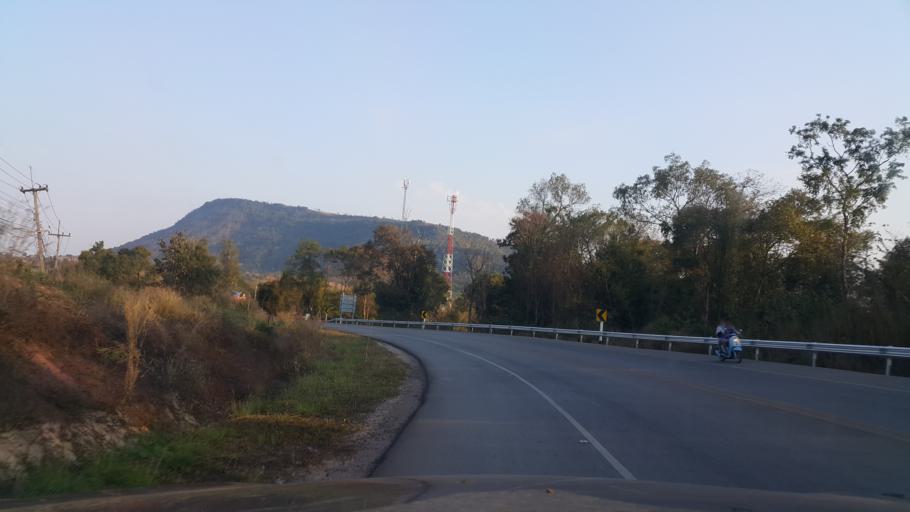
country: TH
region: Loei
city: Phu Ruea
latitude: 17.4544
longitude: 101.4994
